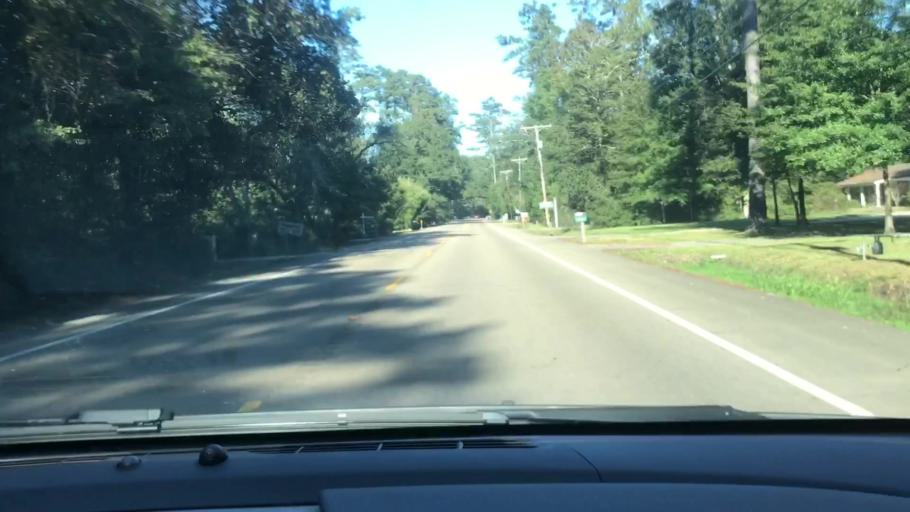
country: US
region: Louisiana
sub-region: Saint Tammany Parish
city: Abita Springs
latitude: 30.5147
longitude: -90.0529
